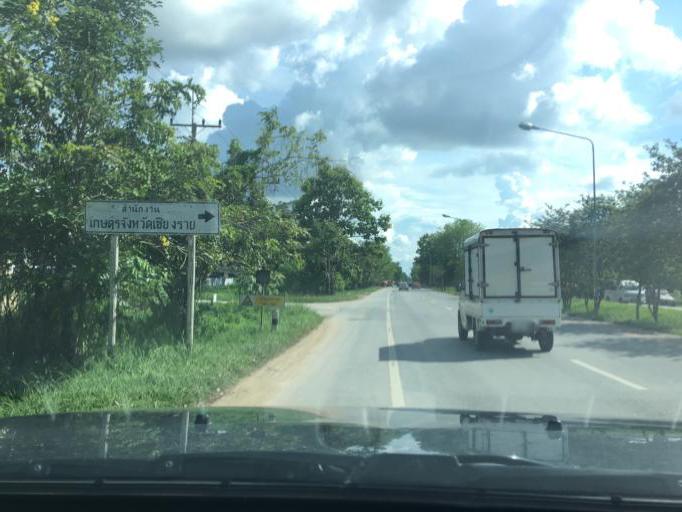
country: TH
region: Chiang Rai
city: Chiang Rai
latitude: 19.8577
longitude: 99.8173
